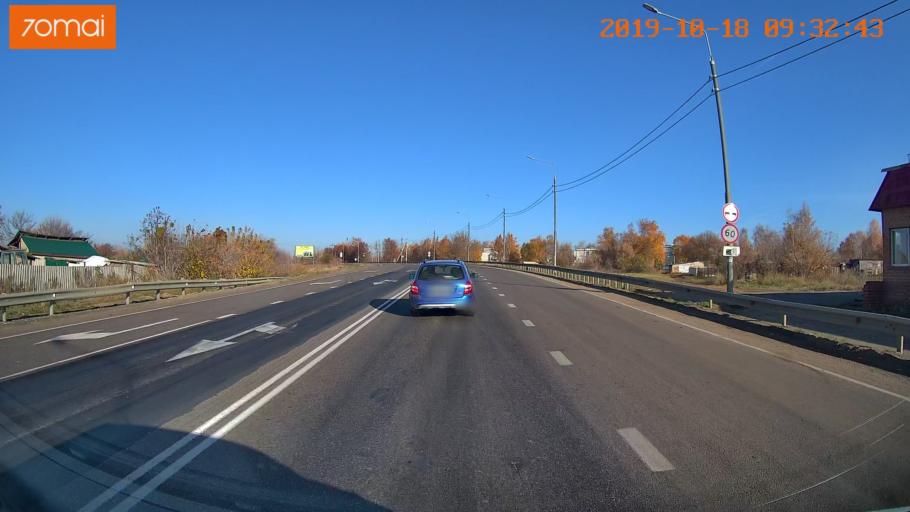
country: RU
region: Tula
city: Yefremov
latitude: 53.1611
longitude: 38.1550
